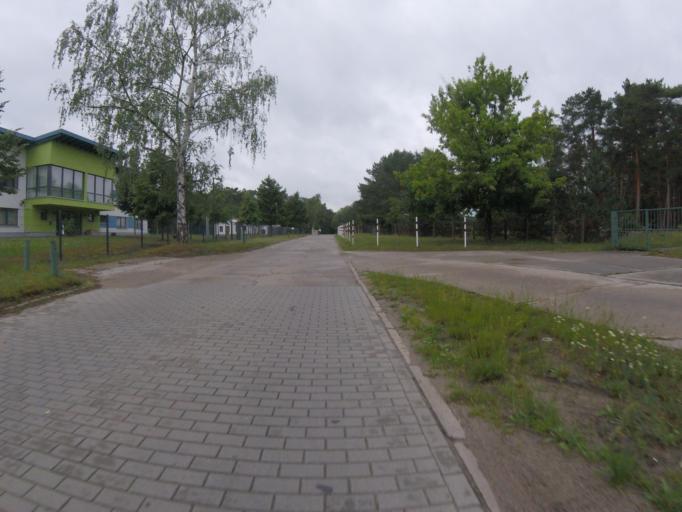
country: DE
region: Brandenburg
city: Konigs Wusterhausen
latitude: 52.2710
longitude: 13.6089
